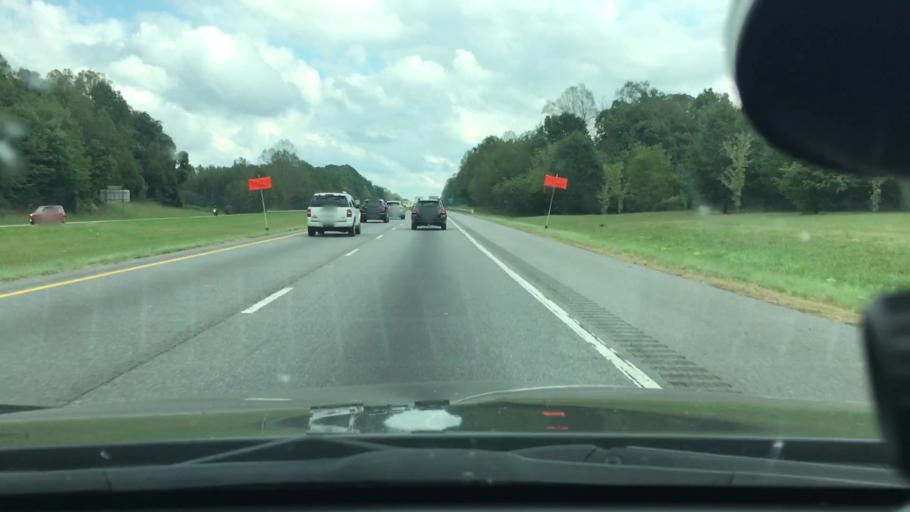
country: US
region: North Carolina
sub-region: Catawba County
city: Conover
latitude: 35.7064
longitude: -81.2469
